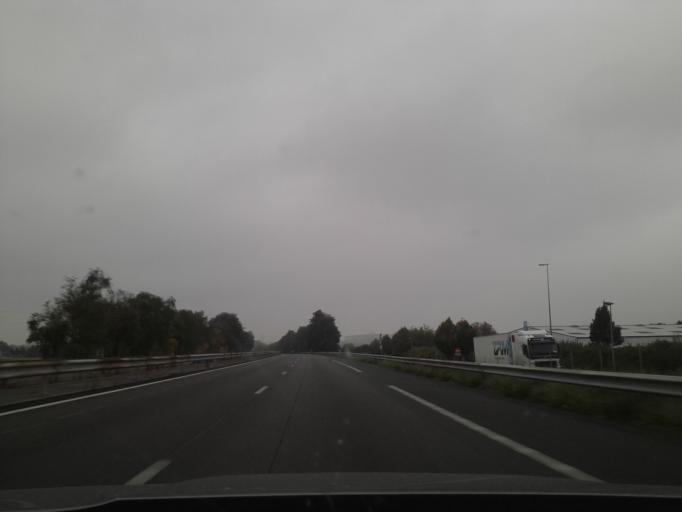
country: FR
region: Nord-Pas-de-Calais
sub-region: Departement du Nord
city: Neuville-Saint-Remy
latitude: 50.1887
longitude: 3.1952
